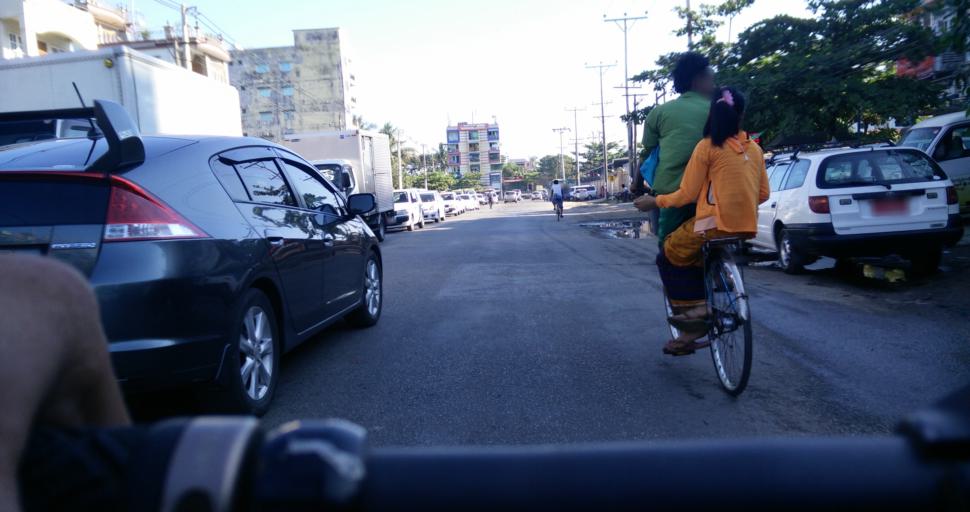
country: MM
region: Yangon
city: Yangon
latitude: 16.8449
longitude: 96.1997
